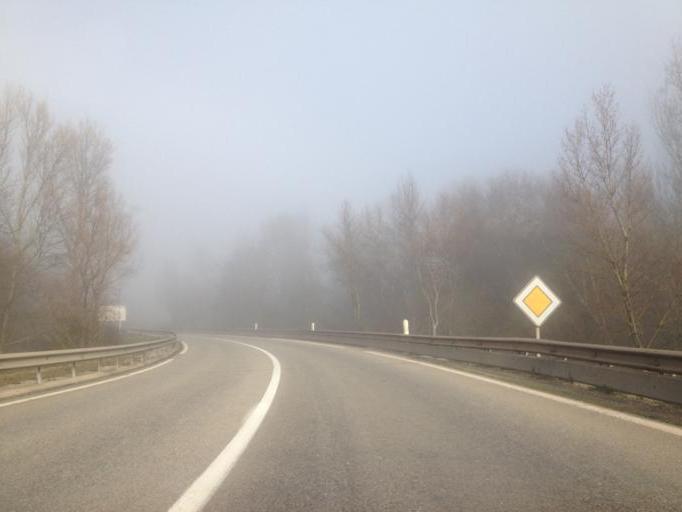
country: FR
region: Rhone-Alpes
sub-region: Departement de l'Ardeche
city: Le Teil
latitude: 44.5243
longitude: 4.6925
